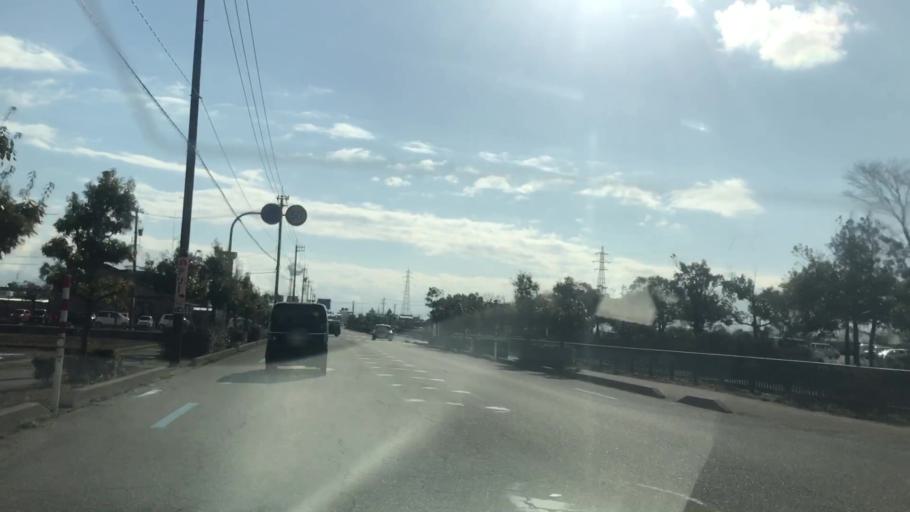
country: JP
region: Toyama
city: Takaoka
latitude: 36.7213
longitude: 137.0136
